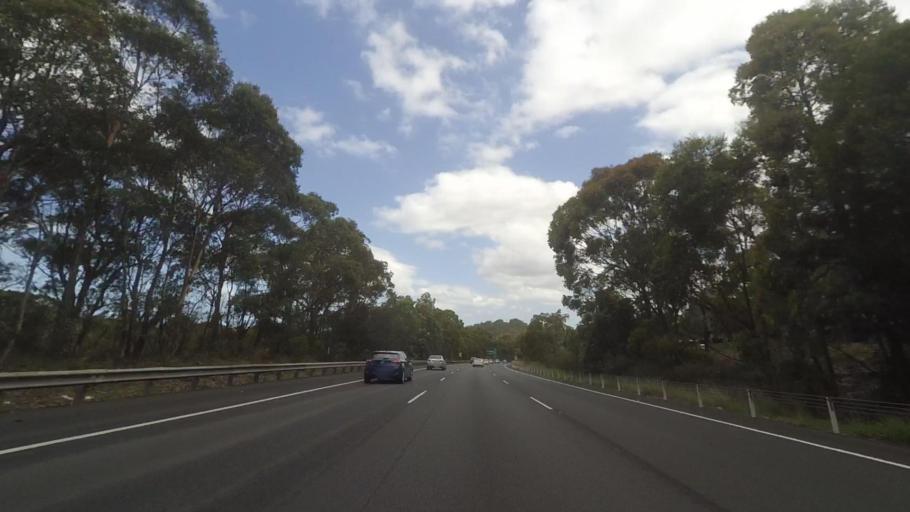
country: AU
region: New South Wales
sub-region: Hornsby Shire
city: Berowra Heights
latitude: -33.5062
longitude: 151.1894
